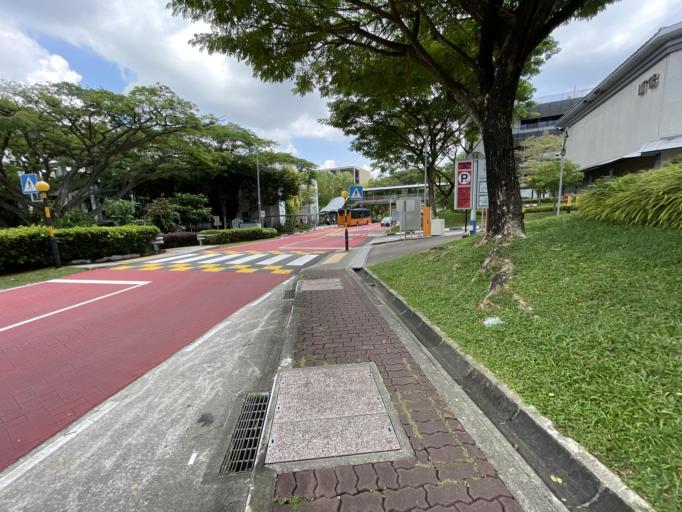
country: SG
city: Singapore
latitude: 1.2948
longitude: 103.7706
